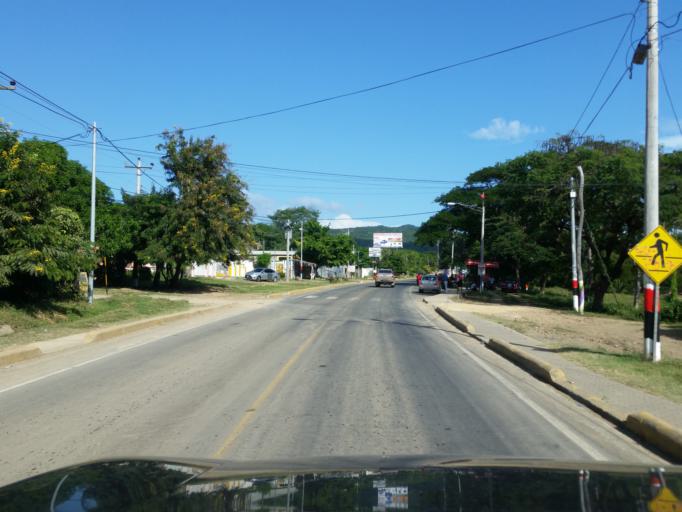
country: NI
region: Rivas
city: San Juan del Sur
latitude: 11.2624
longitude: -85.8586
